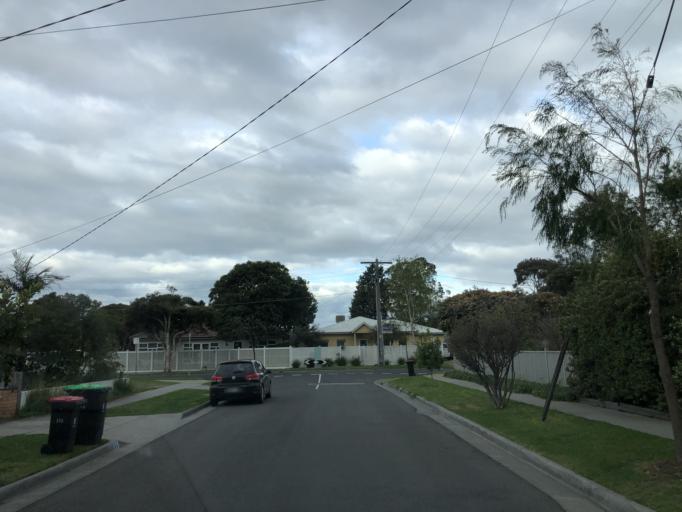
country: AU
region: Victoria
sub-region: Kingston
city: Bonbeach
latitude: -38.0601
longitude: 145.1311
